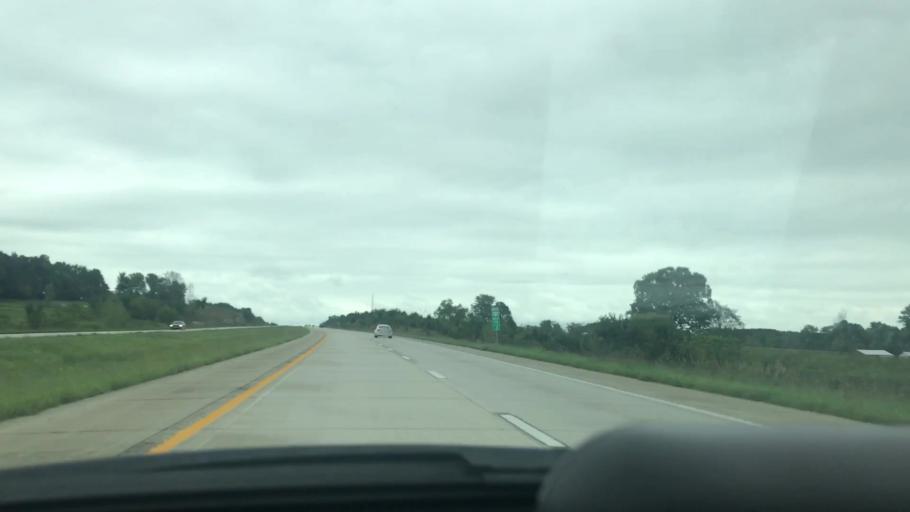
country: US
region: Missouri
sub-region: Dallas County
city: Buffalo
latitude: 37.5318
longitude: -93.1372
